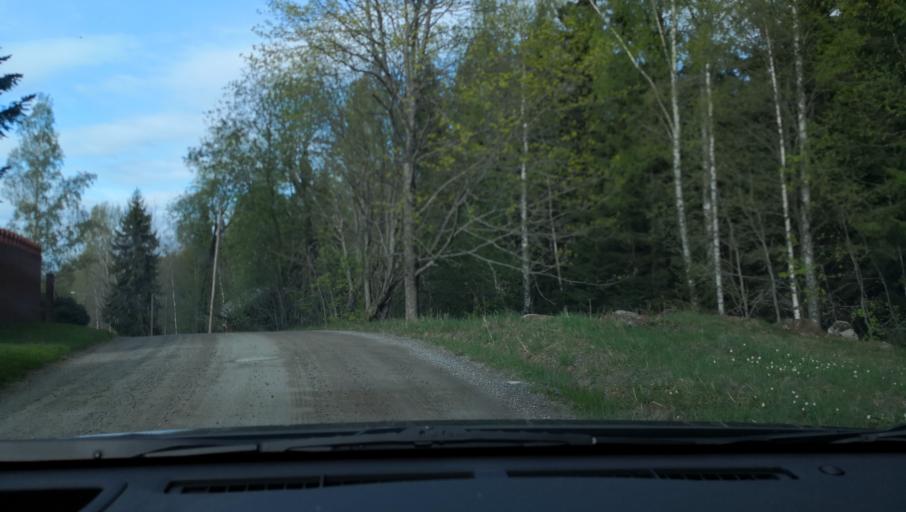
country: SE
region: Dalarna
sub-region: Saters Kommun
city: Saeter
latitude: 60.2634
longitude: 15.8288
